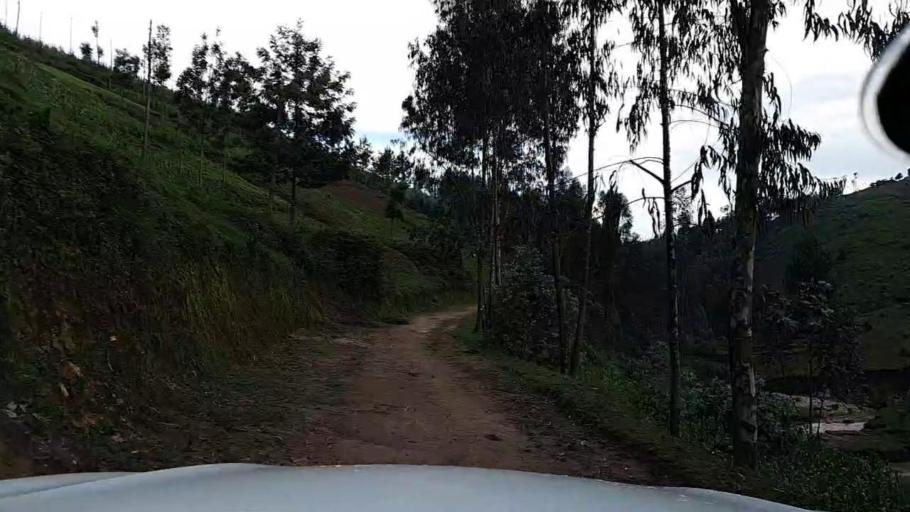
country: BI
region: Kayanza
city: Kayanza
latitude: -2.7762
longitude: 29.4477
